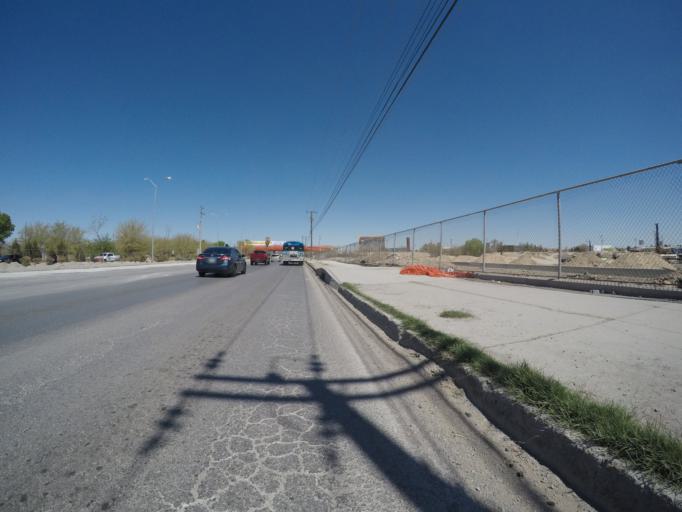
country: MX
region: Chihuahua
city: Ciudad Juarez
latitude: 31.6857
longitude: -106.4244
